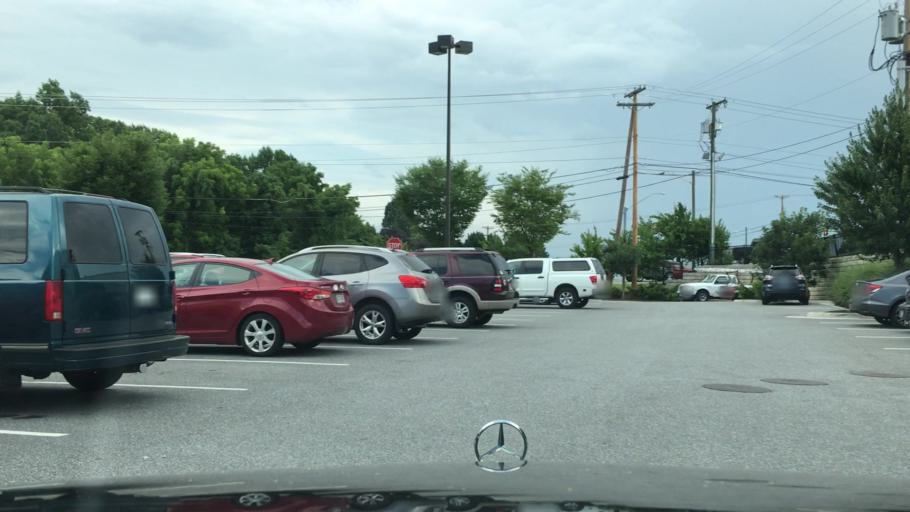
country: US
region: Virginia
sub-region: City of Lynchburg
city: West Lynchburg
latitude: 37.3978
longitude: -79.2232
